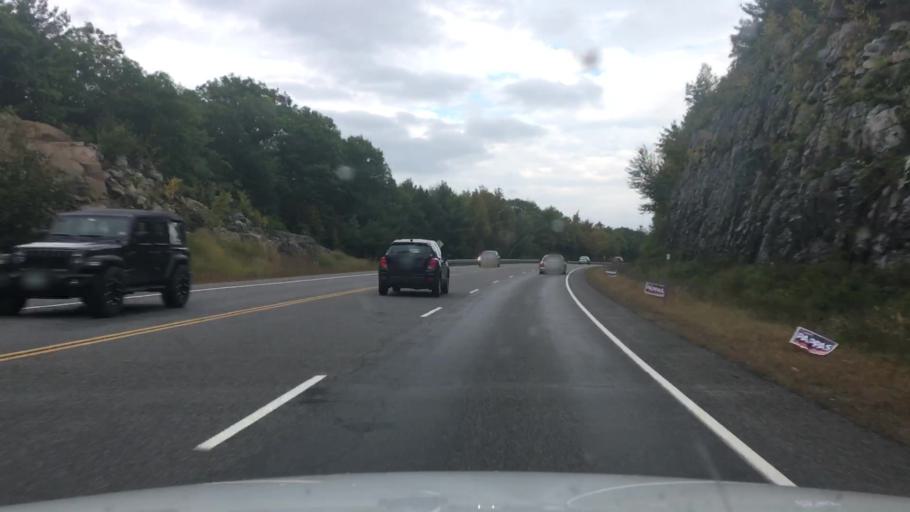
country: US
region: New Hampshire
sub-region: Carroll County
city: Wolfeboro
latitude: 43.5364
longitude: -71.2806
